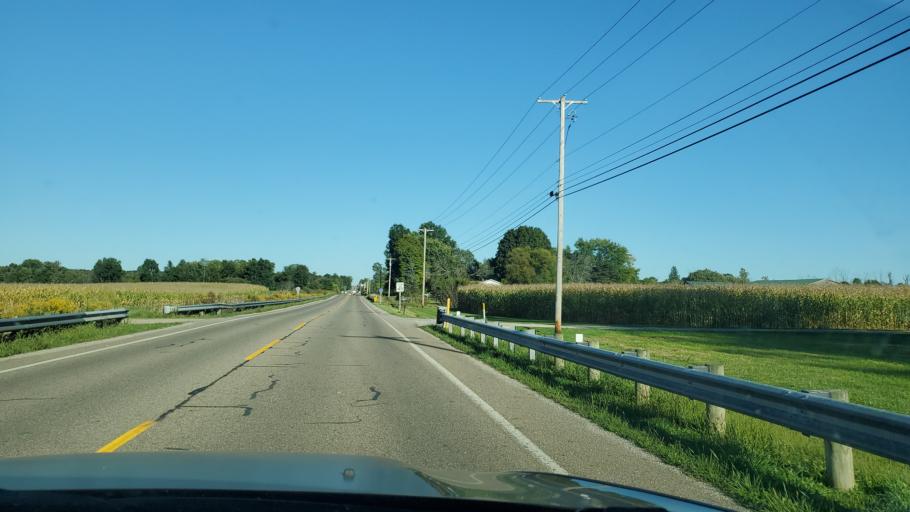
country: US
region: Ohio
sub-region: Mahoning County
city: Canfield
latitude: 40.9882
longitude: -80.7702
